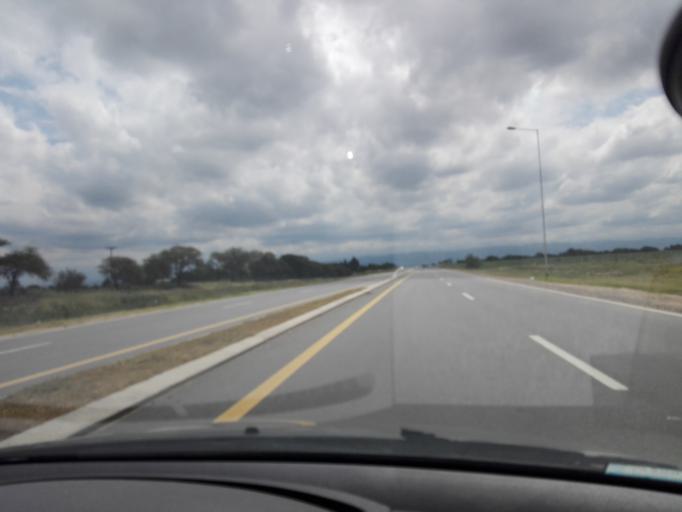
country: AR
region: Cordoba
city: Alta Gracia
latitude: -31.6521
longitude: -64.3187
